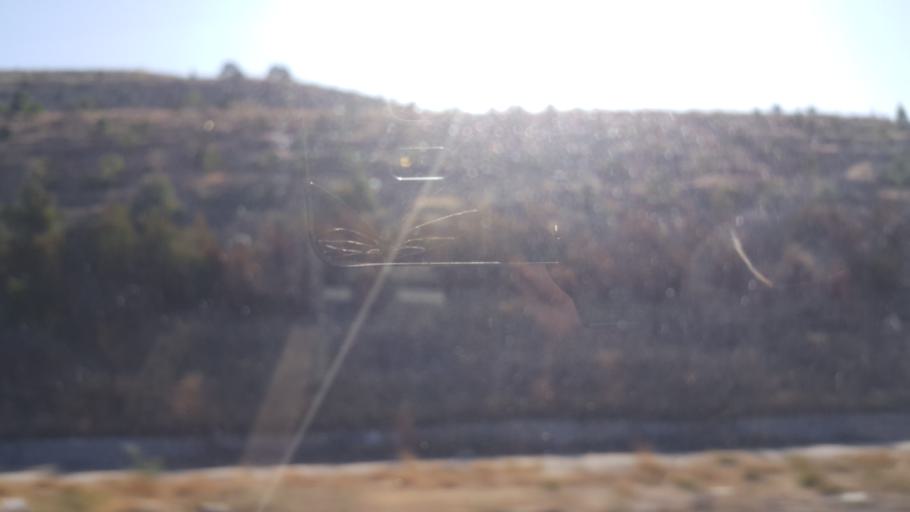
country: TR
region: Ankara
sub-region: Goelbasi
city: Golbasi
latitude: 39.8197
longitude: 32.8759
